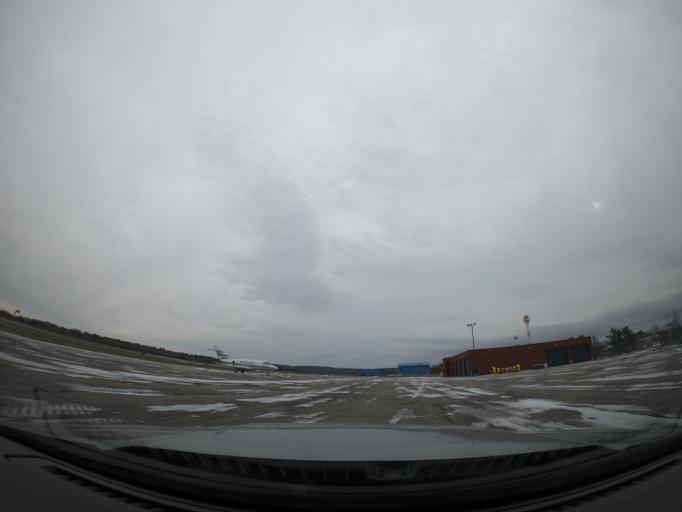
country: US
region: New York
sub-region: Tompkins County
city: Northeast Ithaca
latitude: 42.4890
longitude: -76.4593
